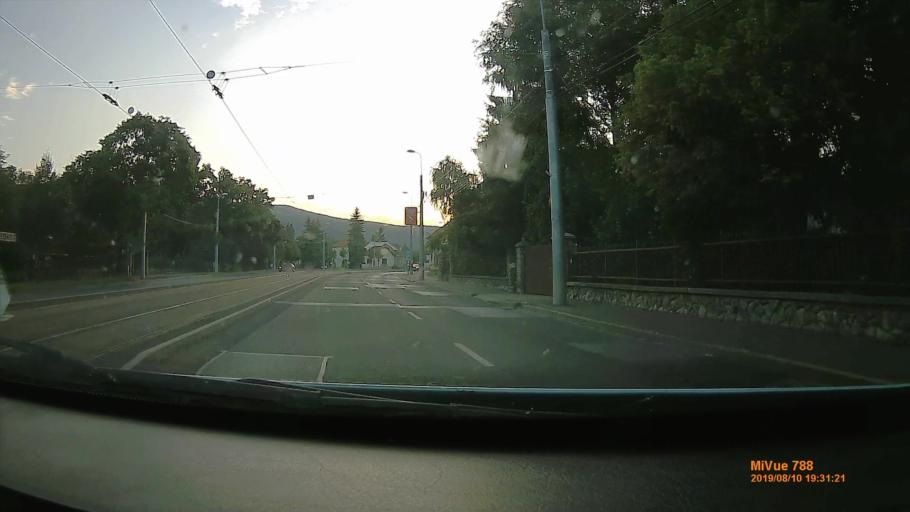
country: HU
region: Borsod-Abauj-Zemplen
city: Sajobabony
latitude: 48.0996
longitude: 20.6948
